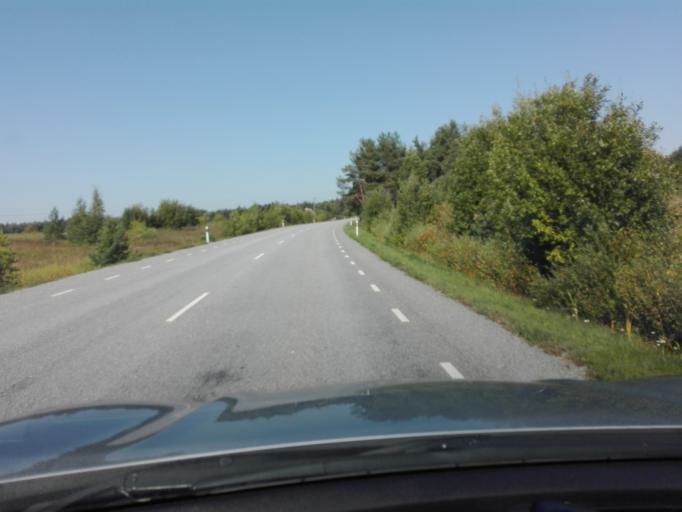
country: EE
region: Raplamaa
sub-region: Rapla vald
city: Rapla
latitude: 58.9975
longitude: 24.7692
